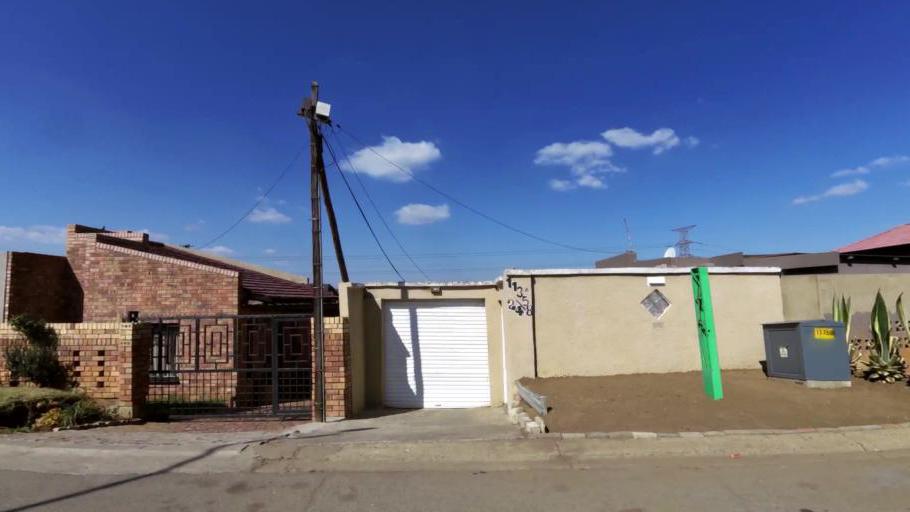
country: ZA
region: Gauteng
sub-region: City of Johannesburg Metropolitan Municipality
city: Soweto
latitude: -26.2452
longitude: 27.9047
